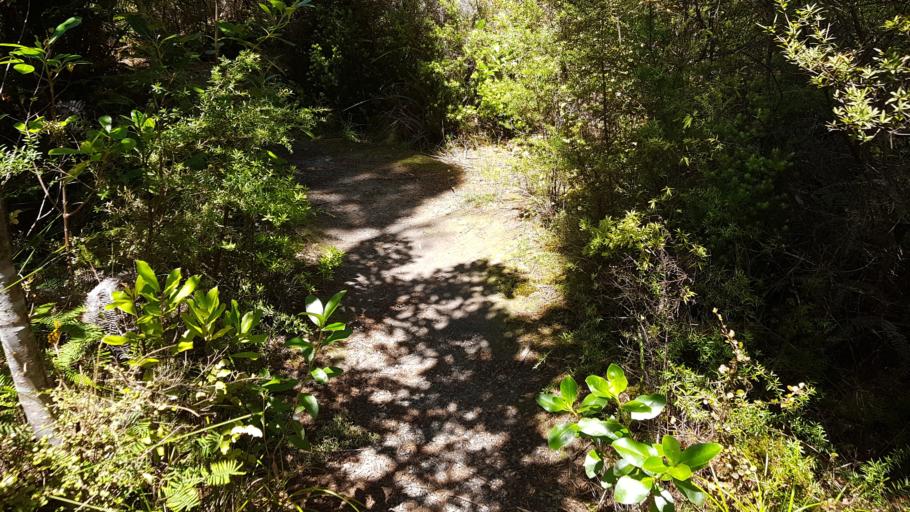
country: NZ
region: Auckland
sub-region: Auckland
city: North Shore
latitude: -36.8225
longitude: 174.7091
